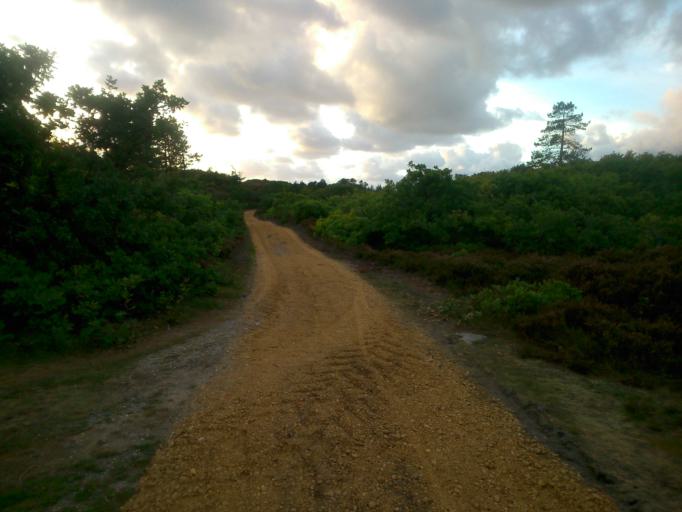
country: DK
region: South Denmark
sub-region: Varde Kommune
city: Oksbol
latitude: 55.6913
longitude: 8.1836
